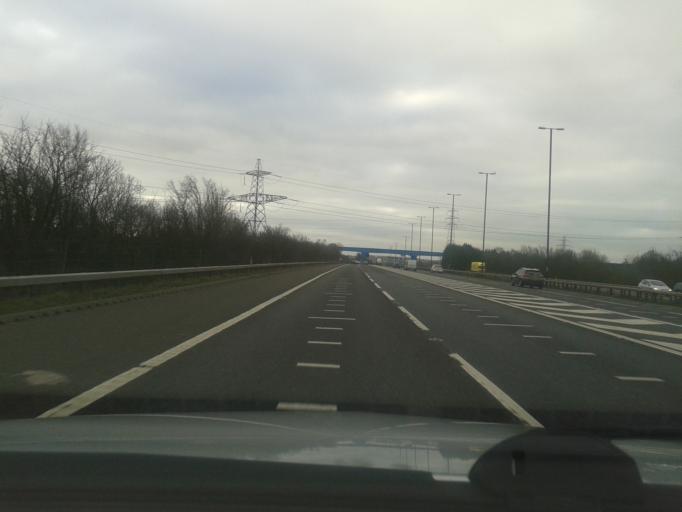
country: GB
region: England
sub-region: South Gloucestershire
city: Winterbourne
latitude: 51.5185
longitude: -2.5219
